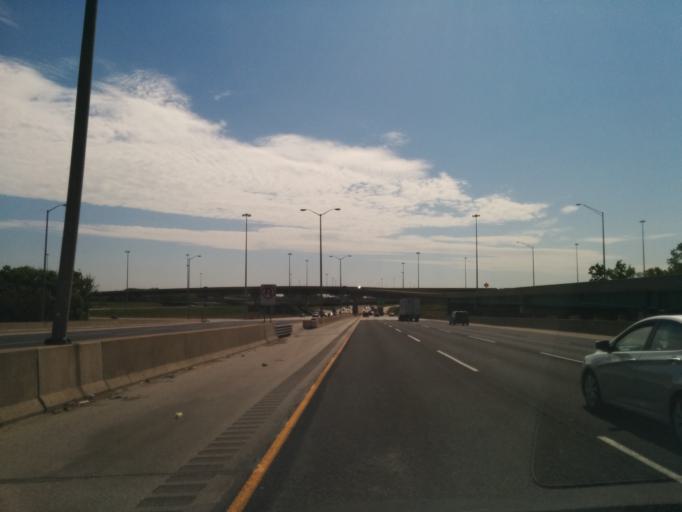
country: US
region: Illinois
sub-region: Cook County
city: Thornton
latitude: 41.5777
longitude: -87.5872
